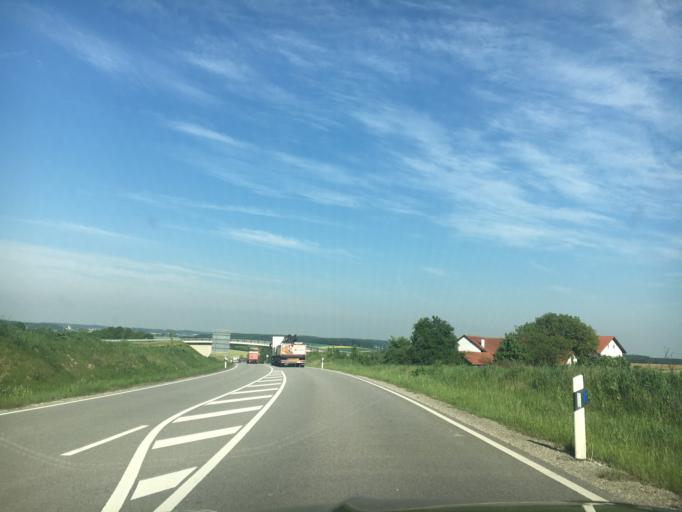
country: DE
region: Bavaria
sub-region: Upper Bavaria
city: Neumarkt-Sankt Veit
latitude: 48.3446
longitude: 12.5080
